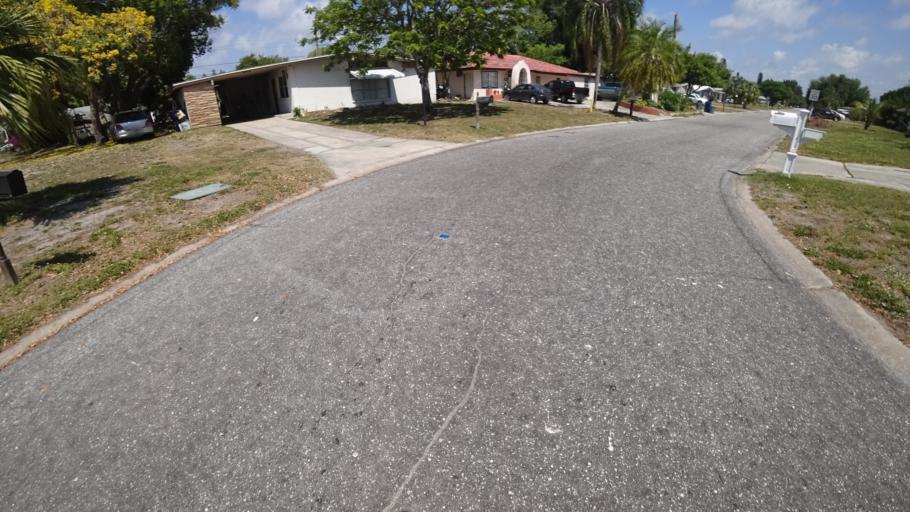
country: US
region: Florida
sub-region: Manatee County
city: Bayshore Gardens
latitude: 27.4304
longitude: -82.5868
